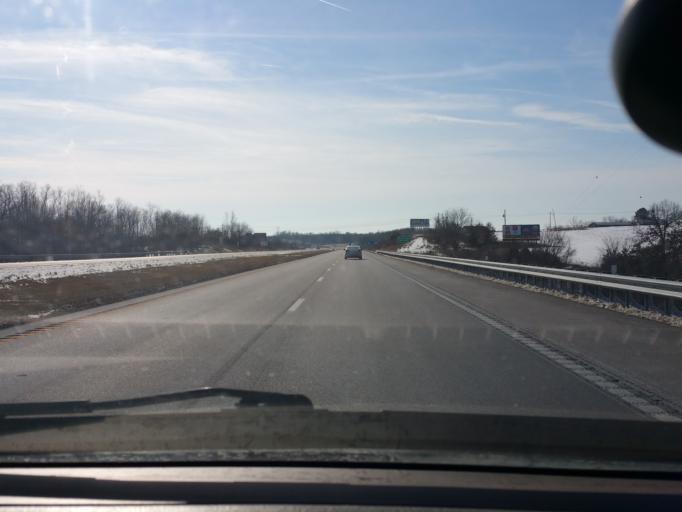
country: US
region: Missouri
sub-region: Clinton County
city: Cameron
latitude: 39.7639
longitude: -94.2167
